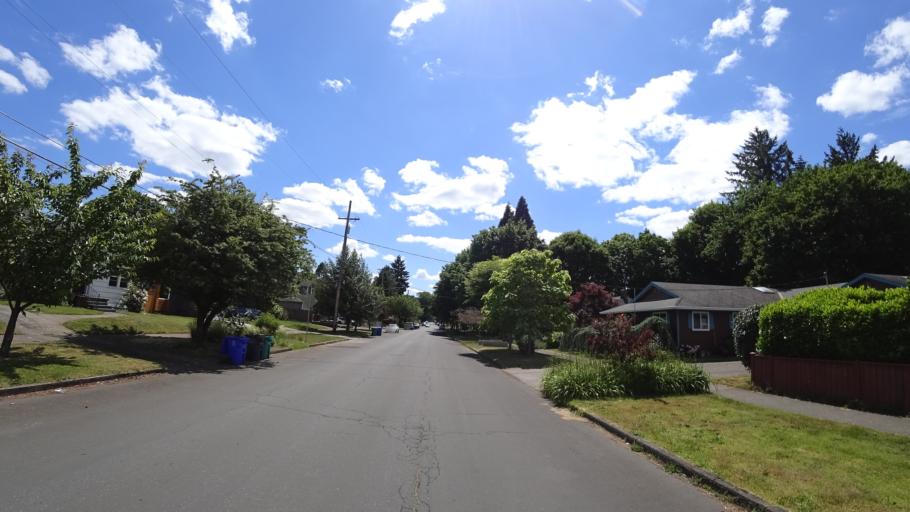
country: US
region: Oregon
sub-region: Washington County
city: West Haven
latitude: 45.5823
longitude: -122.7314
